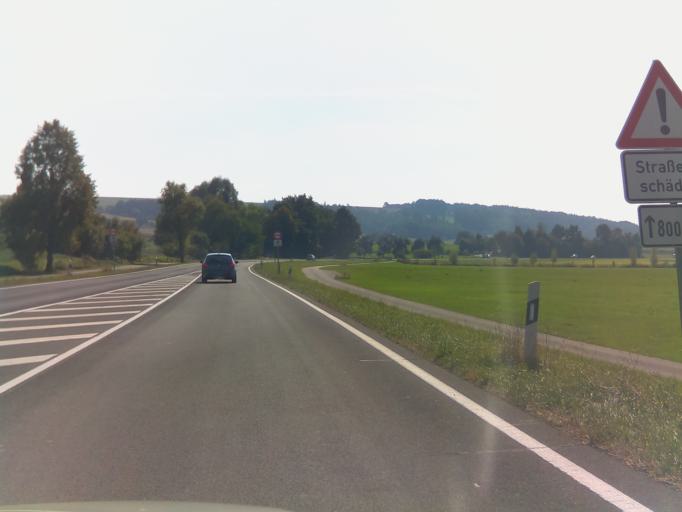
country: DE
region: Bavaria
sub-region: Regierungsbezirk Unterfranken
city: Untermerzbach
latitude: 50.1321
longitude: 10.8926
